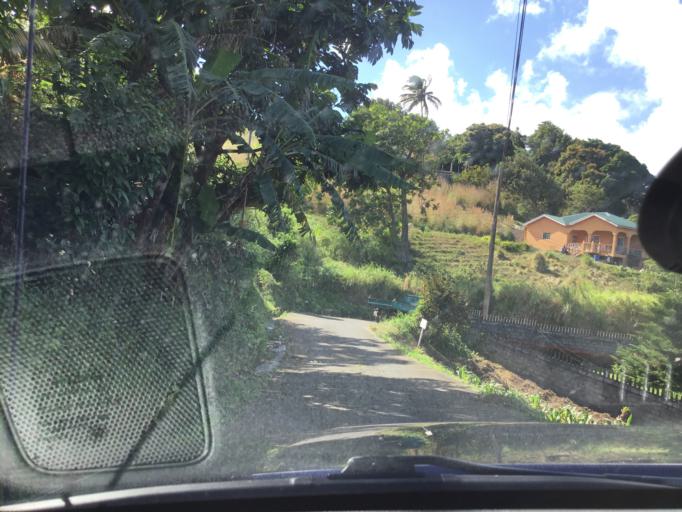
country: VC
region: Charlotte
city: Biabou
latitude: 13.1570
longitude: -61.1675
